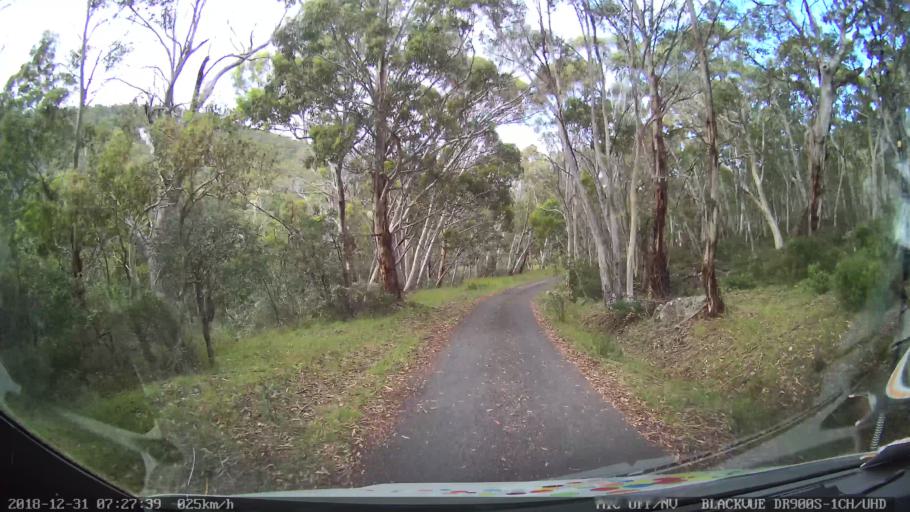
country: AU
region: New South Wales
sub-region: Snowy River
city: Jindabyne
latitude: -36.3218
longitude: 148.4790
